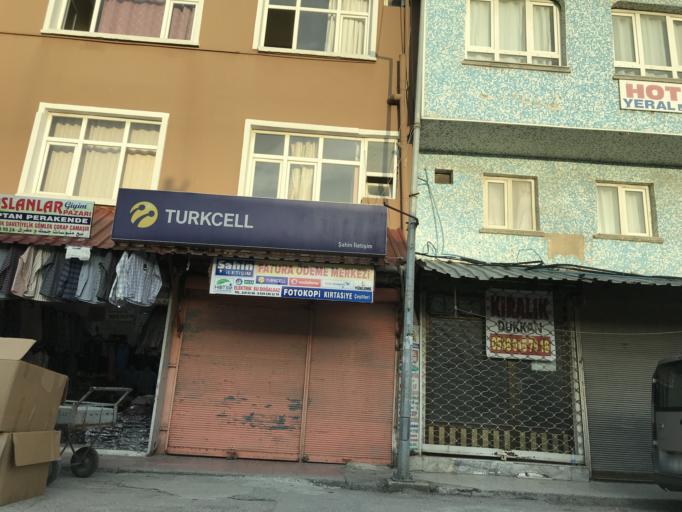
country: TR
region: Hatay
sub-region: Antakya Ilcesi
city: Antakya
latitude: 36.2061
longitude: 36.1654
